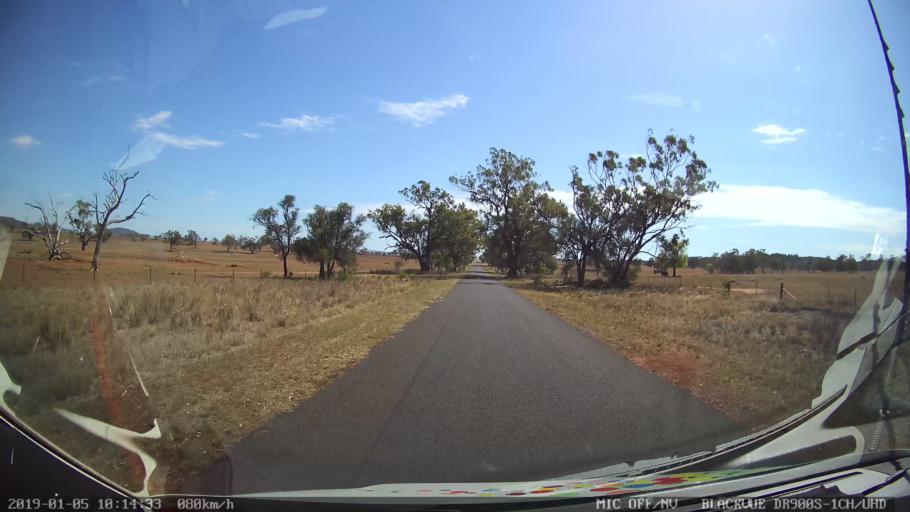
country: AU
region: New South Wales
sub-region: Gilgandra
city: Gilgandra
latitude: -31.5918
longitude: 148.9355
